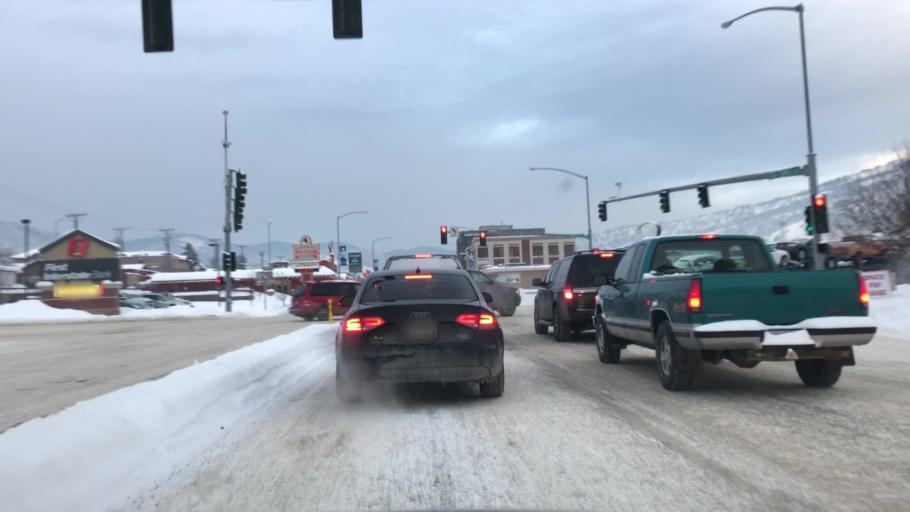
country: US
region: Montana
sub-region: Lewis and Clark County
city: Helena
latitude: 46.5985
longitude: -112.0316
